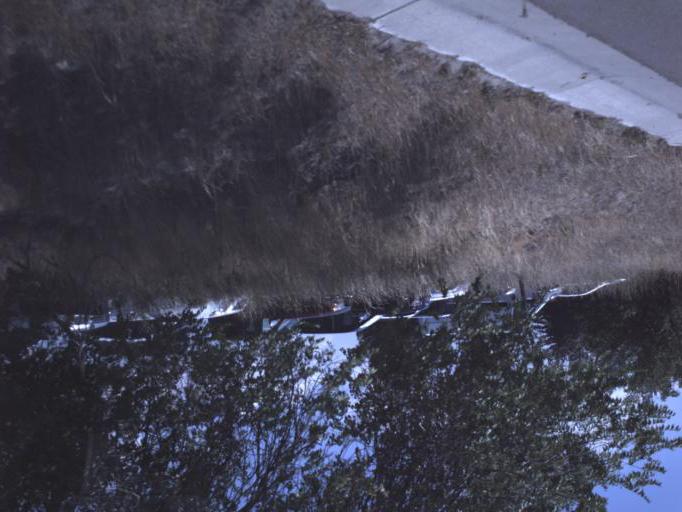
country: US
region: Utah
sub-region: Cache County
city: North Logan
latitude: 41.7439
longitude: -111.7954
